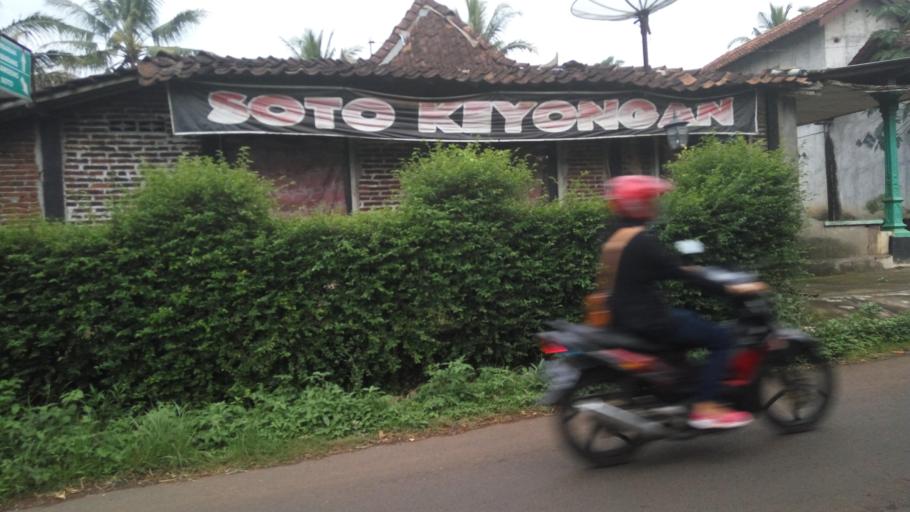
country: ID
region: Central Java
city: Ambarawa
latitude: -7.2422
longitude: 110.4233
